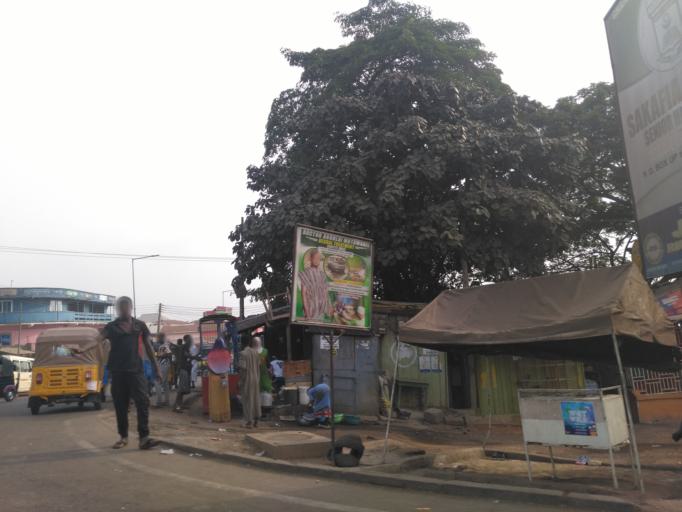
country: GH
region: Ashanti
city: Kumasi
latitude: 6.6970
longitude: -1.5935
